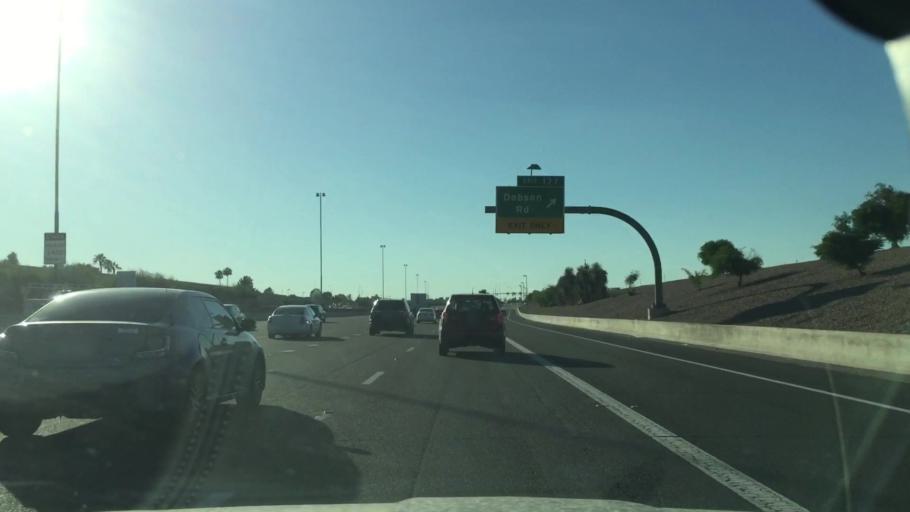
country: US
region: Arizona
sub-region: Maricopa County
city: San Carlos
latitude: 33.3865
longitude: -111.8674
